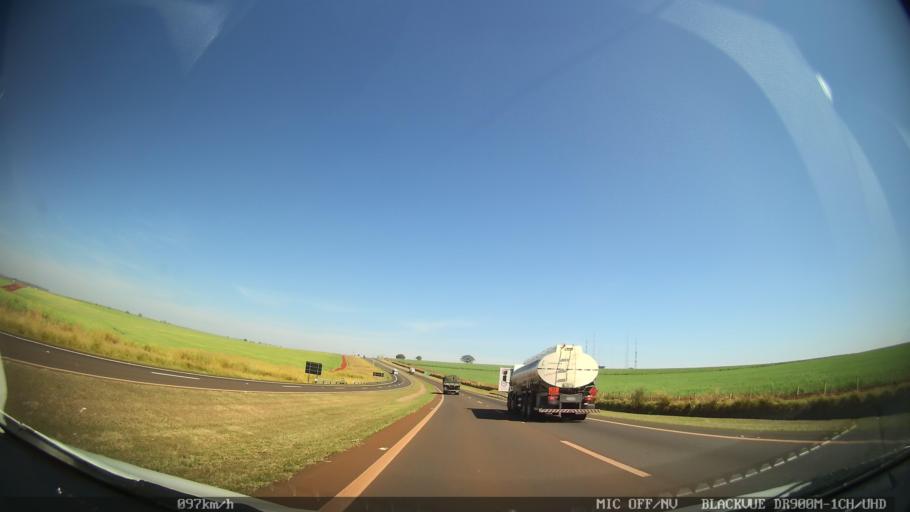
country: BR
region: Sao Paulo
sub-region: Ribeirao Preto
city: Ribeirao Preto
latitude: -21.1542
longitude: -47.8912
